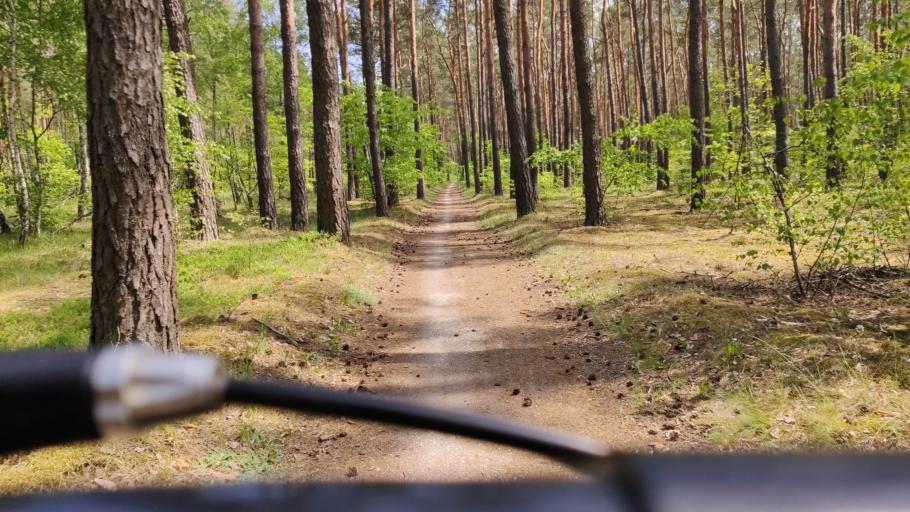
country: PL
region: Kujawsko-Pomorskie
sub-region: Wloclawek
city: Wloclawek
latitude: 52.6343
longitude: 19.1277
